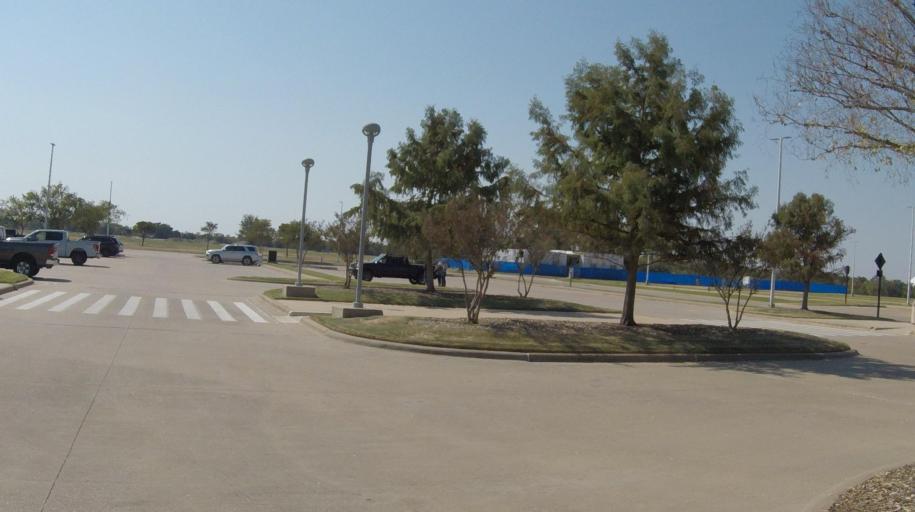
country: US
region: Texas
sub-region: Brazos County
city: College Station
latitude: 30.5968
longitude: -96.3549
